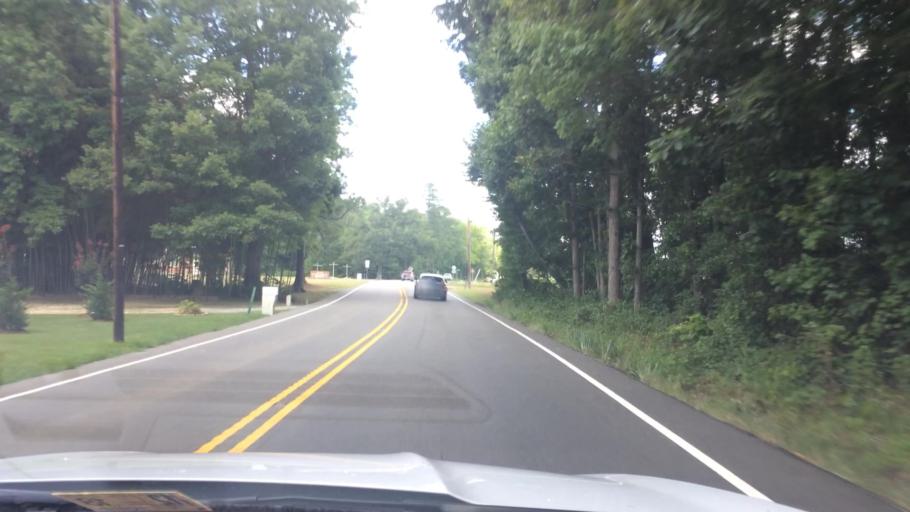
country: US
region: Virginia
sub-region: King William County
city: West Point
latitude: 37.6055
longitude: -76.7734
